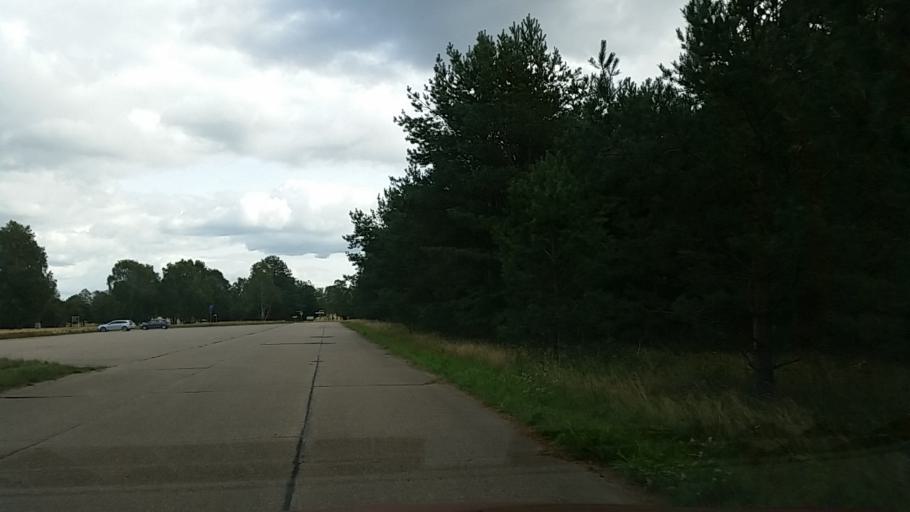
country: DE
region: Lower Saxony
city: Schneverdingen
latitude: 53.1503
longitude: 9.8104
